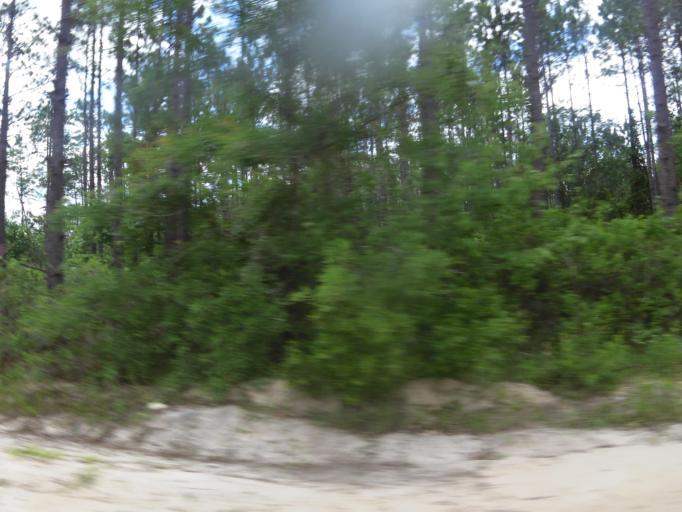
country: US
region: Florida
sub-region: Clay County
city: Asbury Lake
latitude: 29.8988
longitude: -81.8315
